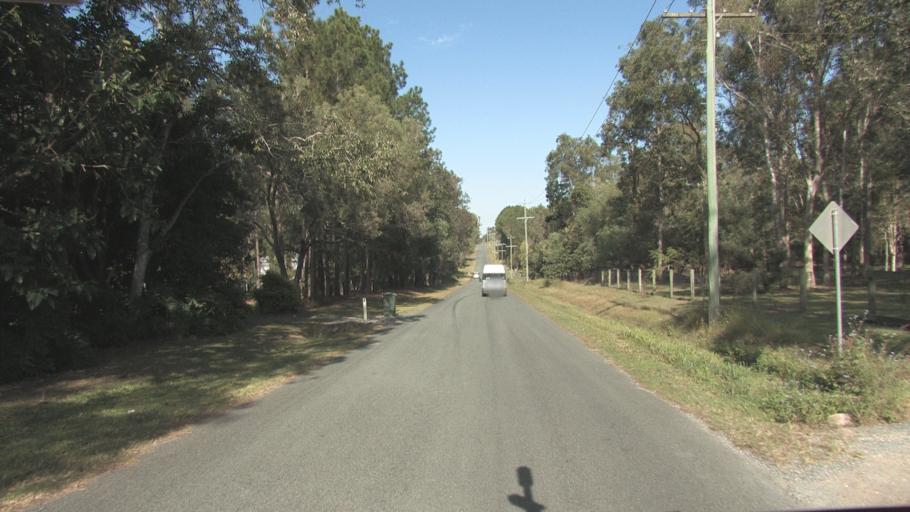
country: AU
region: Queensland
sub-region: Logan
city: North Maclean
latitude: -27.7731
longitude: 152.9918
